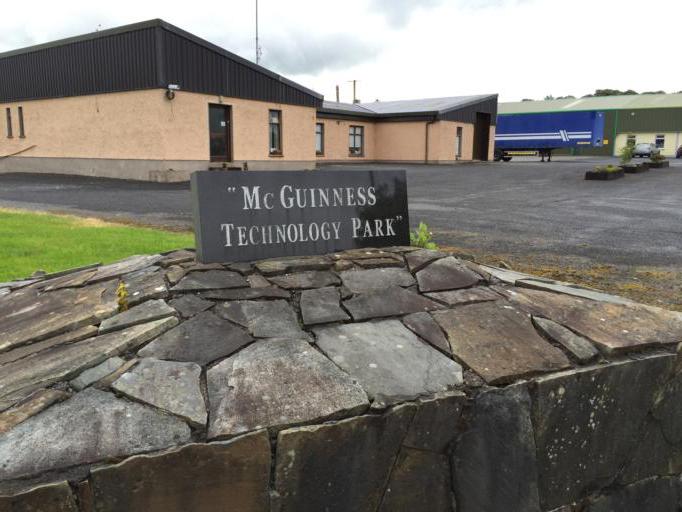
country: IE
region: Connaught
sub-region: Maigh Eo
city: Swinford
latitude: 54.0385
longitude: -8.8944
